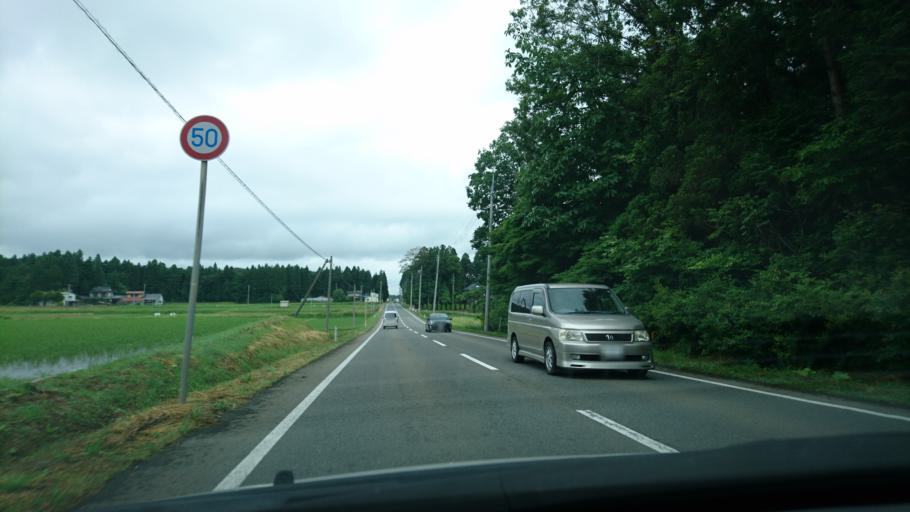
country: JP
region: Iwate
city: Mizusawa
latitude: 39.1141
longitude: 141.0530
